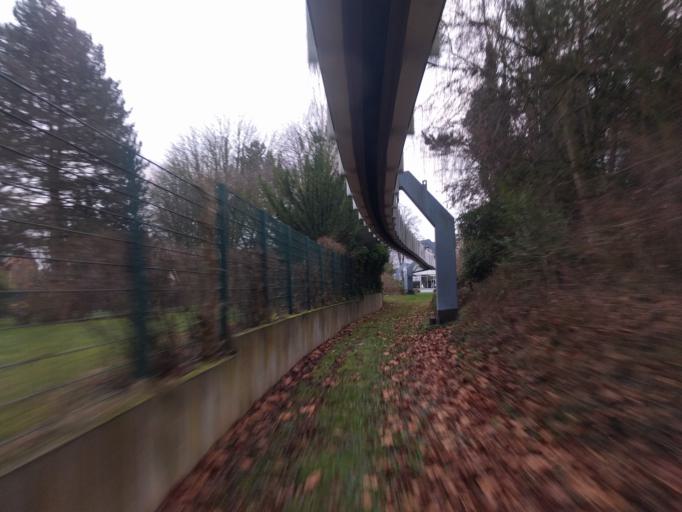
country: DE
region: North Rhine-Westphalia
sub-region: Regierungsbezirk Arnsberg
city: Dortmund
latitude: 51.4825
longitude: 7.4092
